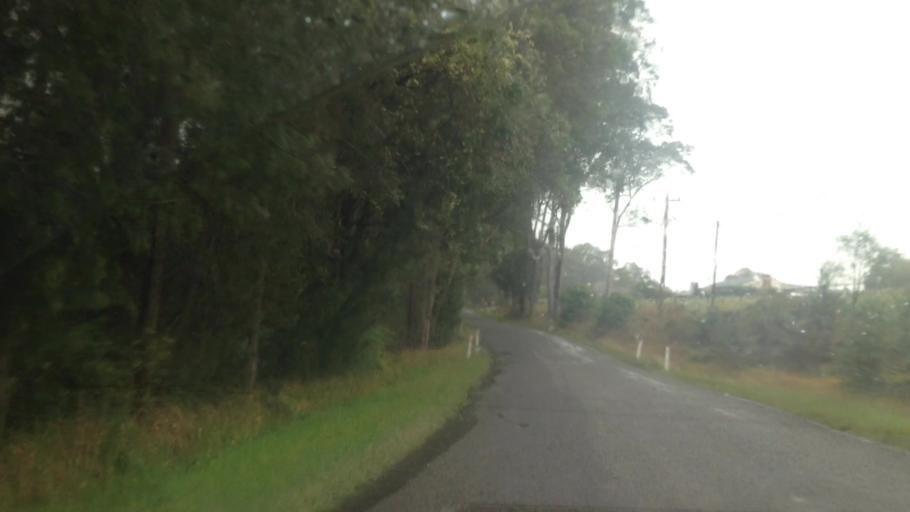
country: AU
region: New South Wales
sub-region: Wyong Shire
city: Little Jilliby
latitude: -33.1991
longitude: 151.3617
